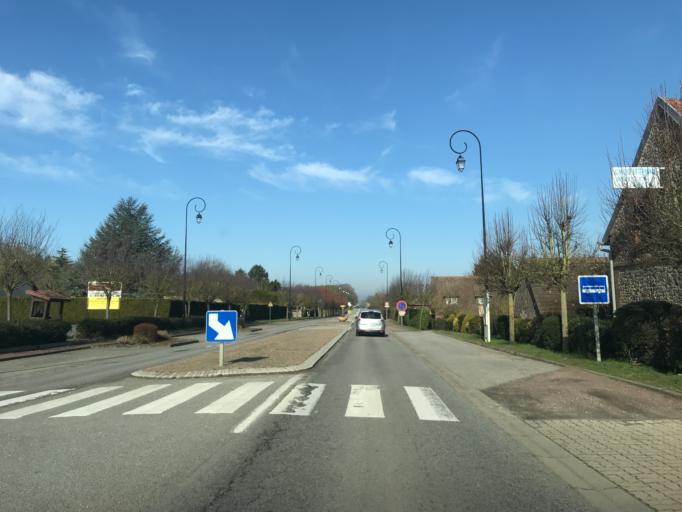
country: FR
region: Haute-Normandie
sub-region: Departement de l'Eure
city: Saint-Pierre-du-Vauvray
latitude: 49.2081
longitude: 1.2251
